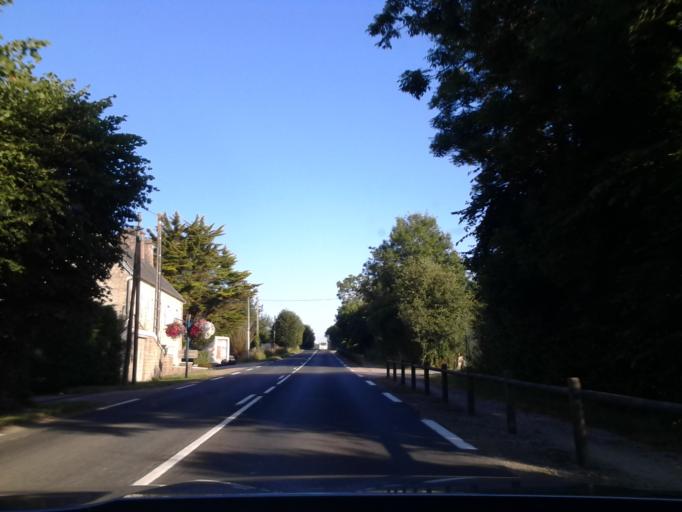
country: FR
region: Lower Normandy
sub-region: Departement de la Manche
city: Valognes
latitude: 49.5147
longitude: -1.4849
